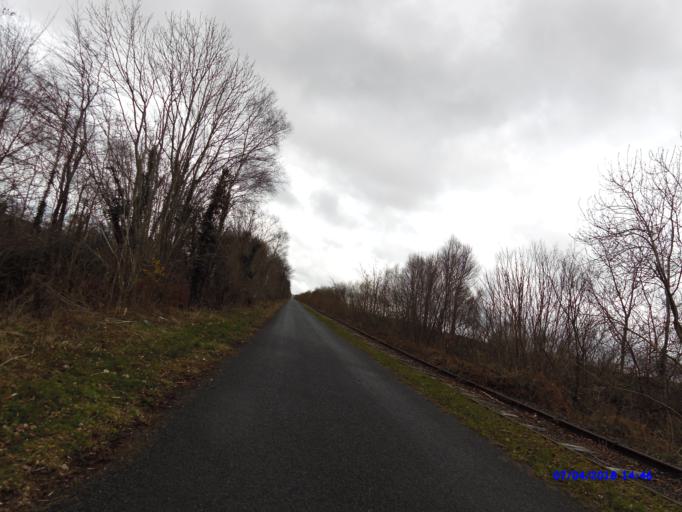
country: IE
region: Leinster
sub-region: An Iarmhi
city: Athlone
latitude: 53.4179
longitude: -7.8746
